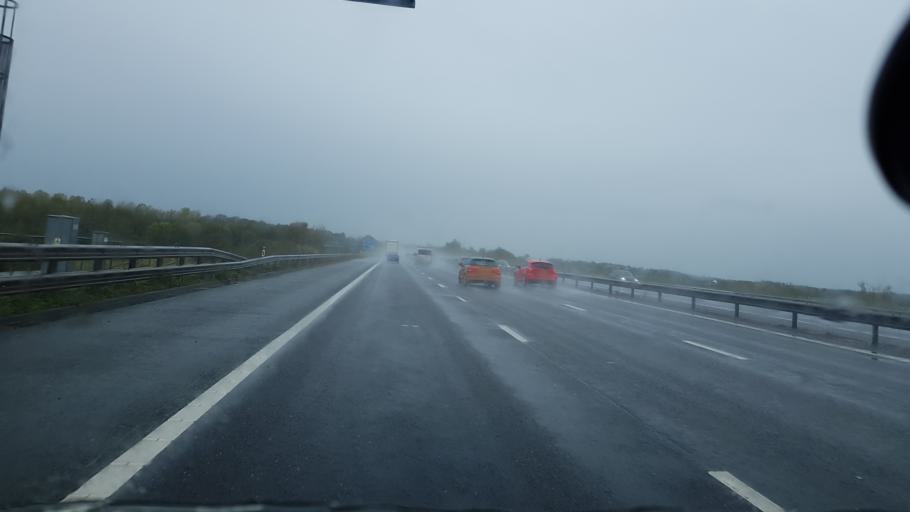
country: GB
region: England
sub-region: Worcestershire
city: Bredon
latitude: 52.0326
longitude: -2.1268
